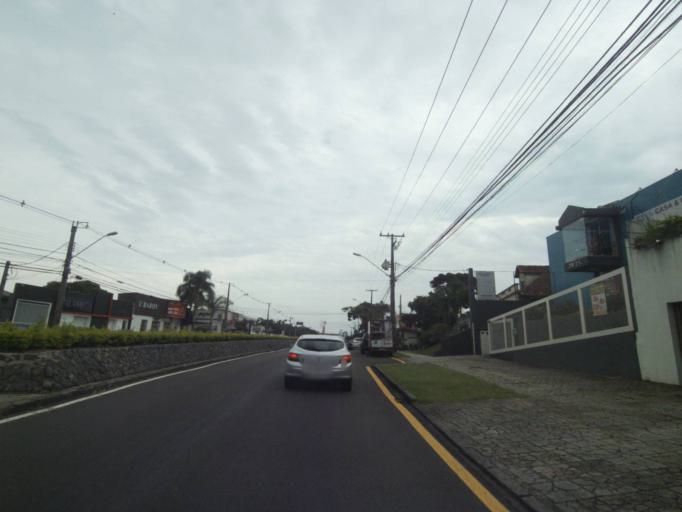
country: BR
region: Parana
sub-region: Curitiba
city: Curitiba
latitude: -25.4164
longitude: -49.2951
